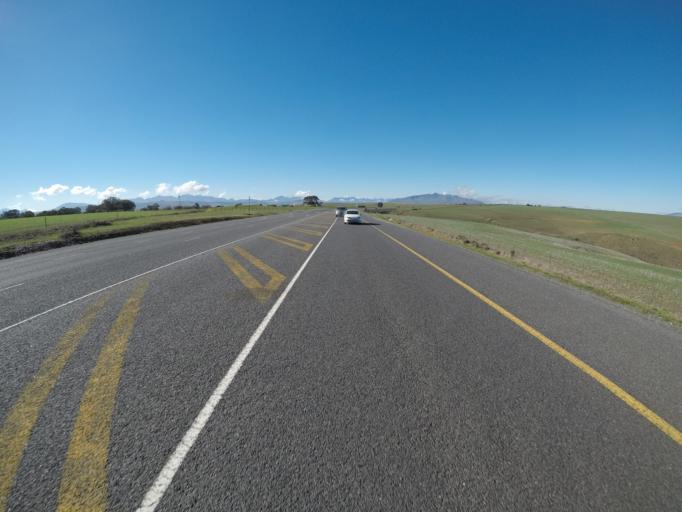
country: ZA
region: Western Cape
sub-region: Overberg District Municipality
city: Caledon
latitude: -34.2235
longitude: 19.2791
